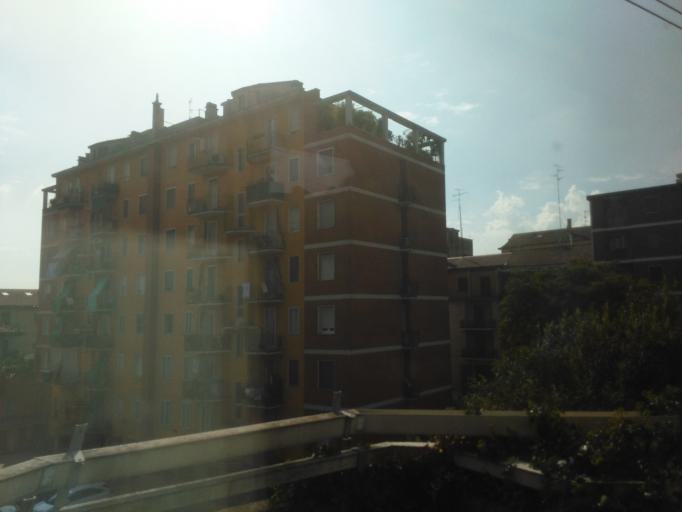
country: IT
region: Lombardy
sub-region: Citta metropolitana di Milano
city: Linate
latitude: 45.4716
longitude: 9.2434
